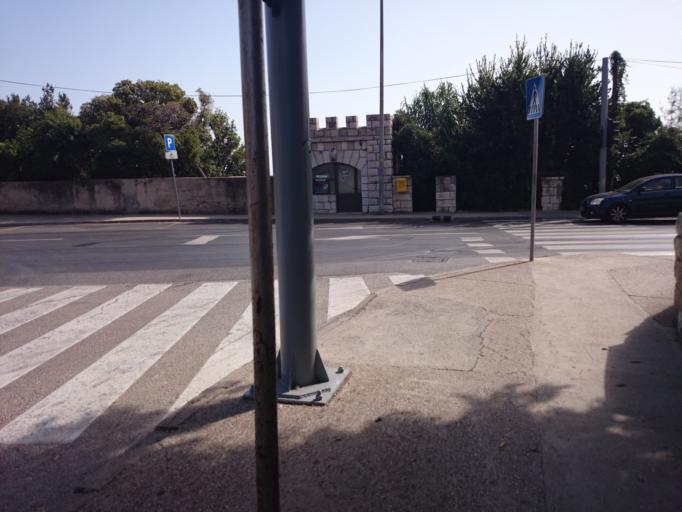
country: HR
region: Dubrovacko-Neretvanska
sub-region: Grad Dubrovnik
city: Dubrovnik
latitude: 42.6470
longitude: 18.0937
